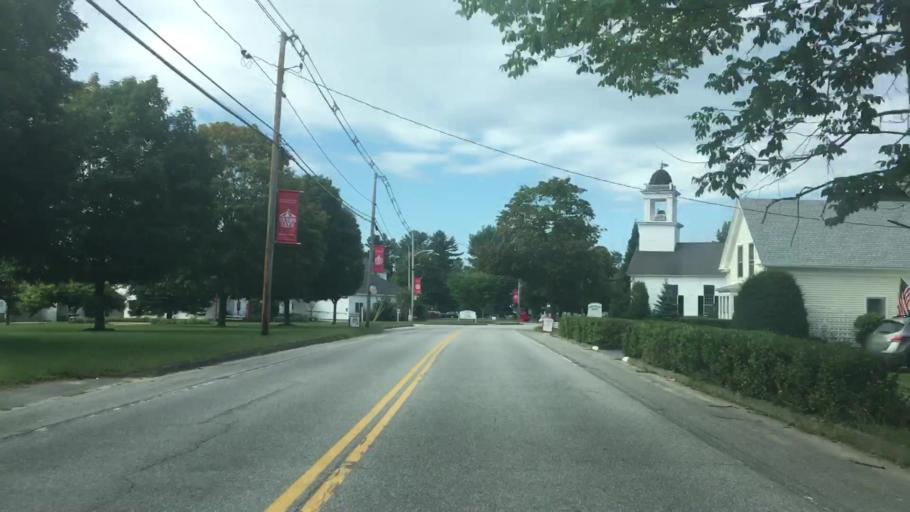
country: US
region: Maine
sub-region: Cumberland County
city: Raymond
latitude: 44.0036
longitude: -70.5218
